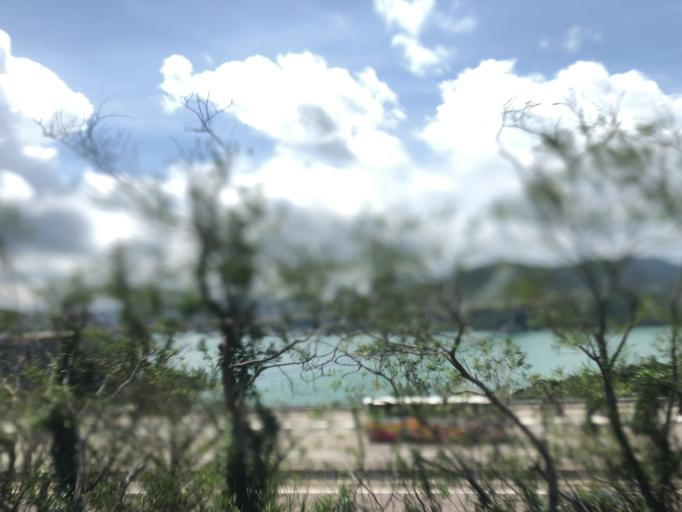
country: HK
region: Tsuen Wan
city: Tsuen Wan
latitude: 22.3677
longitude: 114.0713
